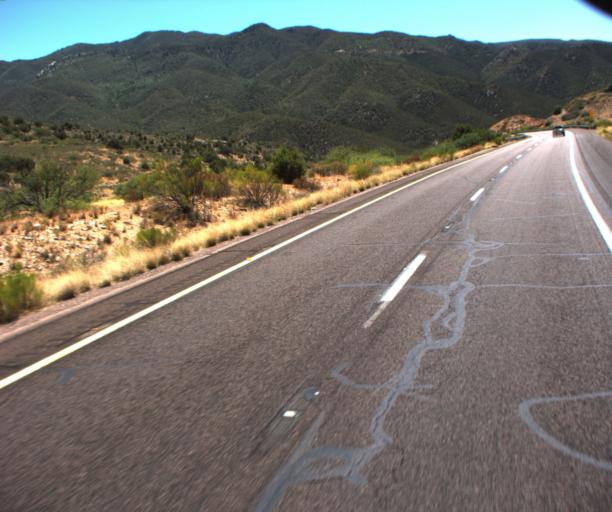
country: US
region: Arizona
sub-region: Gila County
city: Tonto Basin
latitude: 33.9649
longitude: -111.3893
